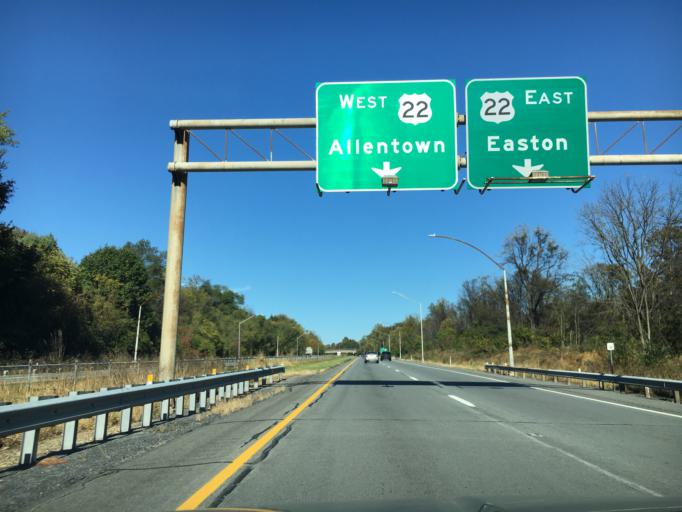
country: US
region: Pennsylvania
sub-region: Lehigh County
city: Fountain Hill
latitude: 40.6340
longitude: -75.4088
